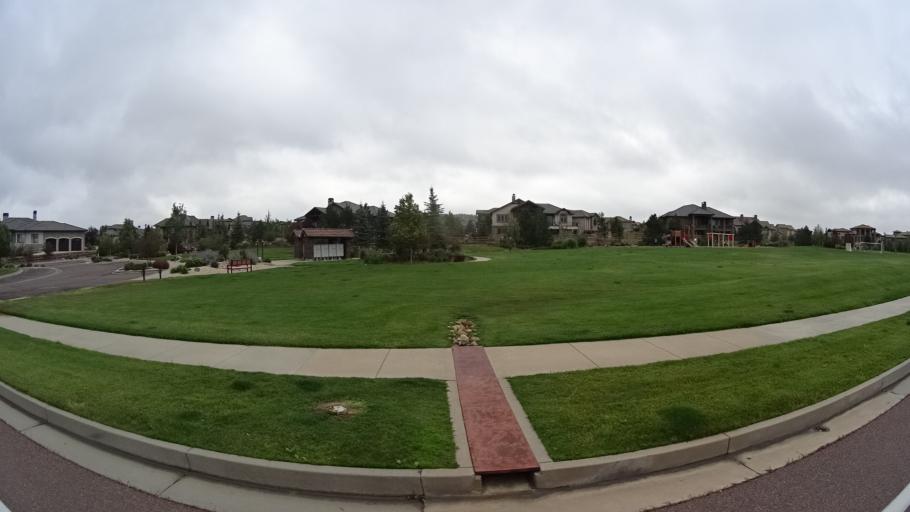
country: US
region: Colorado
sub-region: El Paso County
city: Gleneagle
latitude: 39.0272
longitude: -104.7878
